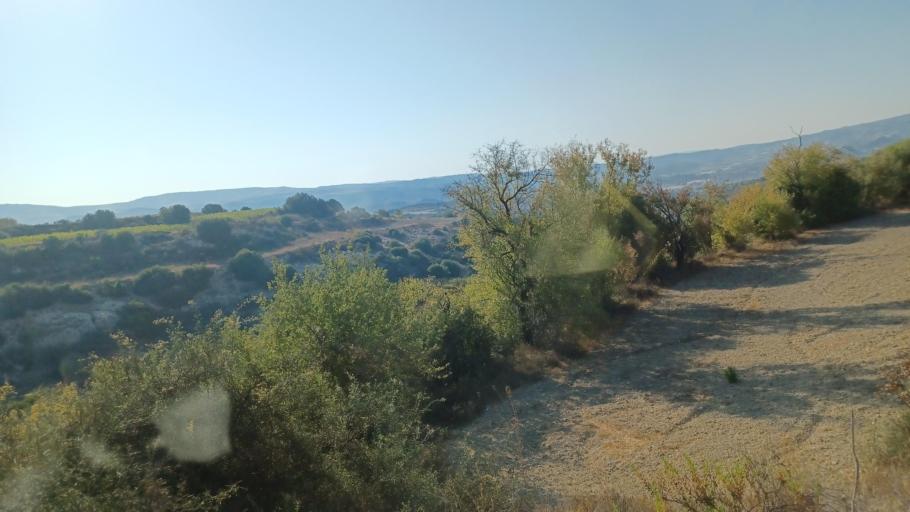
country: CY
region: Pafos
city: Mesogi
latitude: 34.8809
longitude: 32.5226
